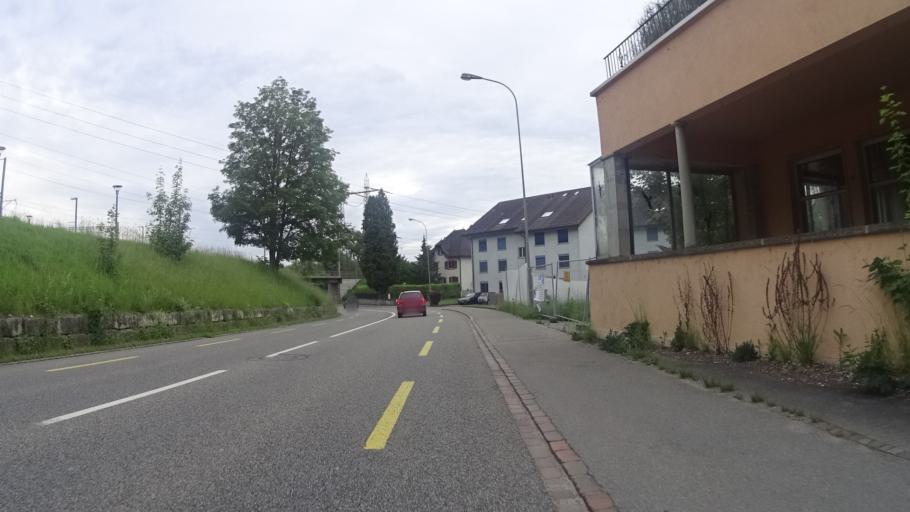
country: CH
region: Aargau
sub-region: Bezirk Zurzach
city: Koblenz
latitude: 47.5992
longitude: 8.2260
